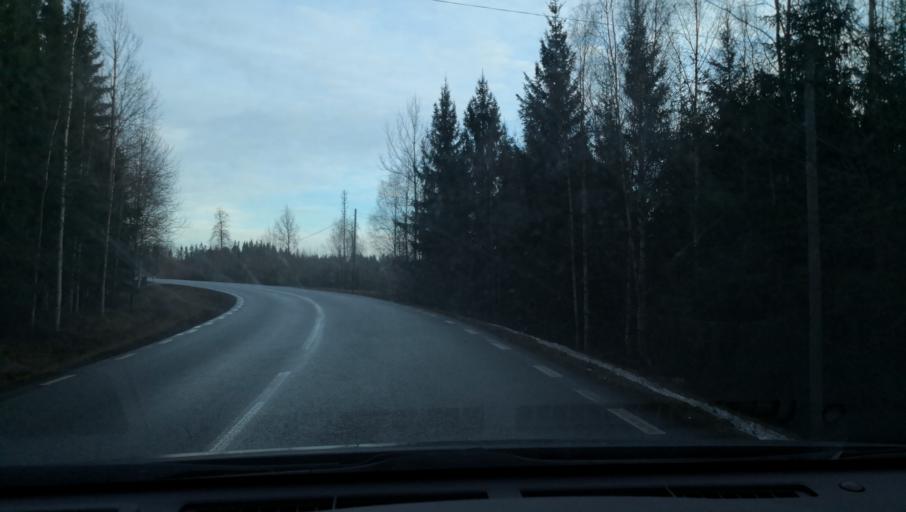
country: SE
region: OErebro
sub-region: Degerfors Kommun
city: Degerfors
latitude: 59.1361
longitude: 14.4601
